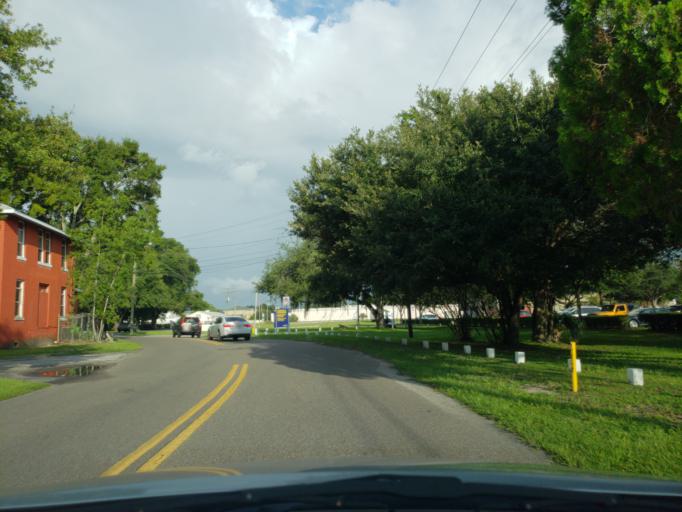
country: US
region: Florida
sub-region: Hillsborough County
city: East Lake-Orient Park
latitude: 27.9994
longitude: -82.4272
